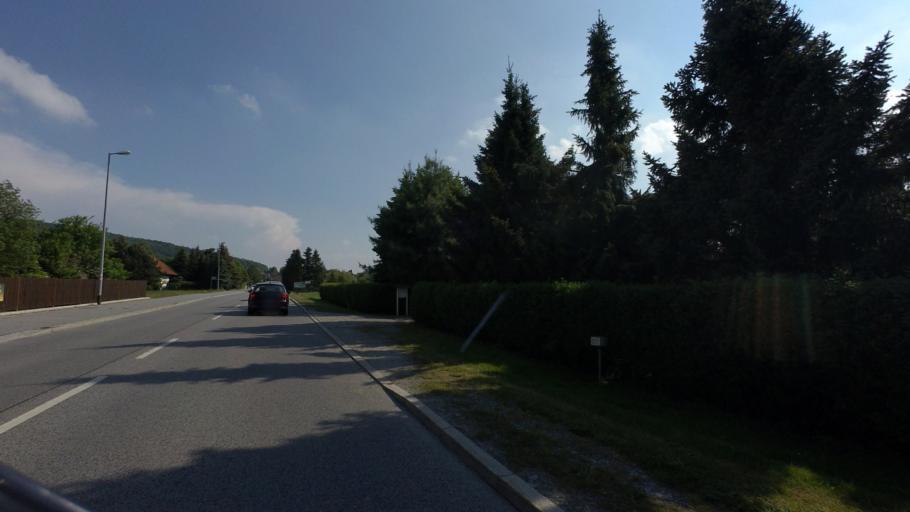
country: DE
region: Saxony
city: Grosspostwitz
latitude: 51.1429
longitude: 14.4407
